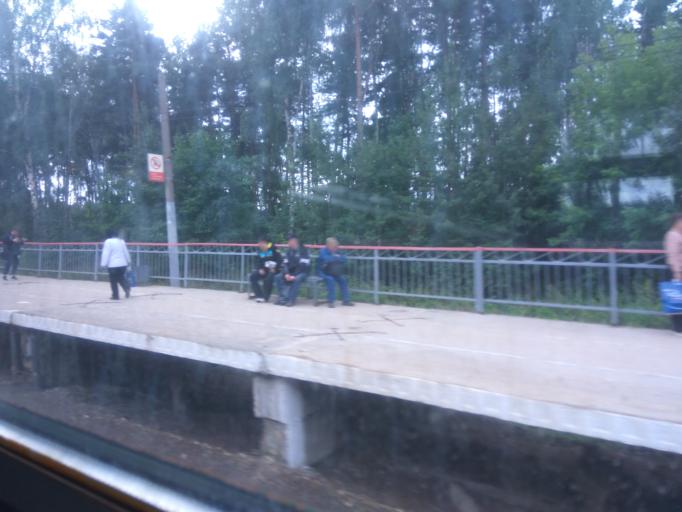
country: RU
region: Moskovskaya
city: Beloozerskiy
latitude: 55.4624
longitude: 38.4486
